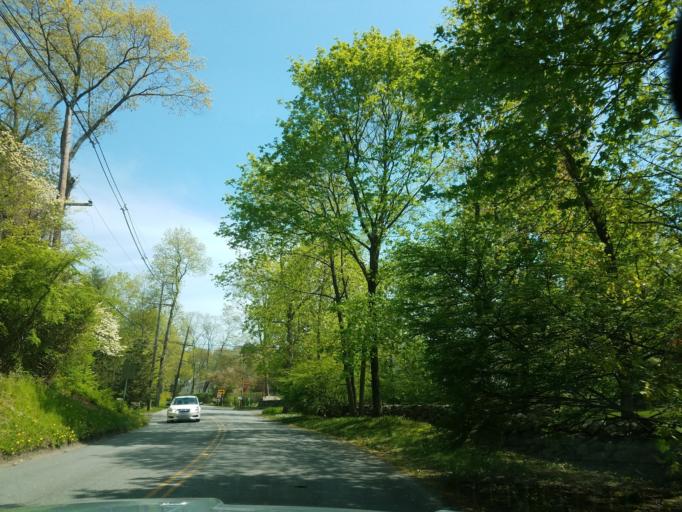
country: US
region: Connecticut
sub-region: Fairfield County
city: New Canaan
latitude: 41.1280
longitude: -73.4753
